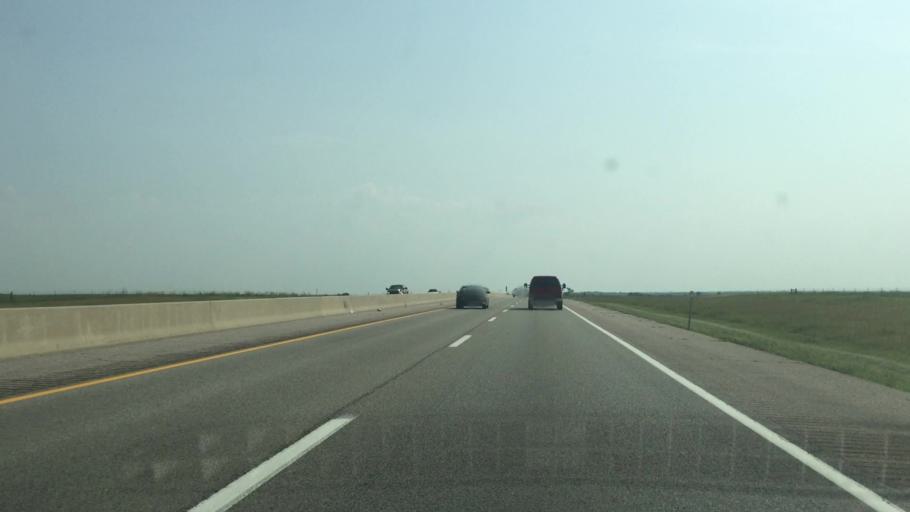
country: US
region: Kansas
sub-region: Butler County
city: El Dorado
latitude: 37.9060
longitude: -96.8211
